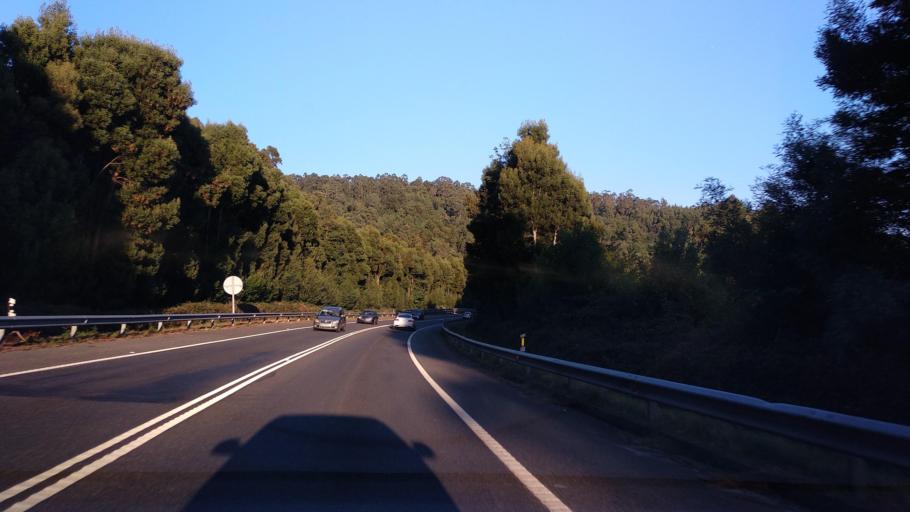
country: ES
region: Galicia
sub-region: Provincia de Pontevedra
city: Moana
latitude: 42.2885
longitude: -8.7748
